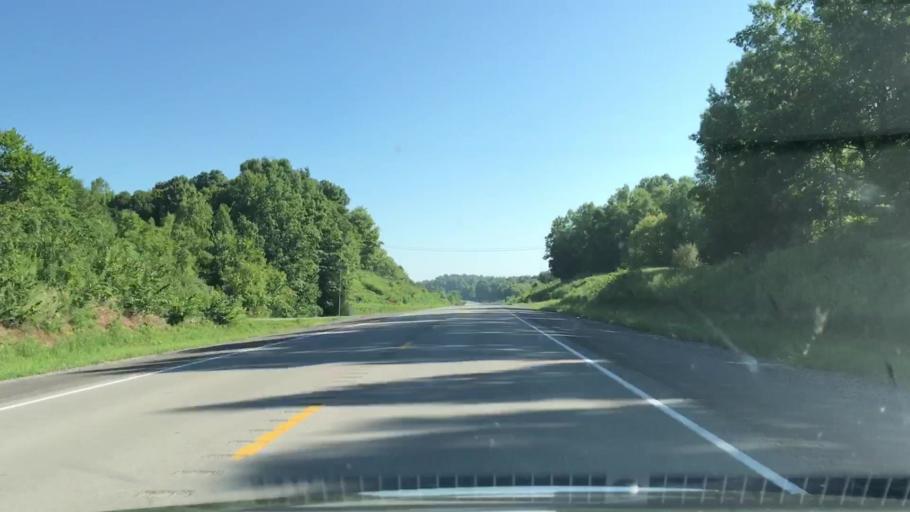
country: US
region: Kentucky
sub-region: Cumberland County
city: Burkesville
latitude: 36.6426
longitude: -85.3844
